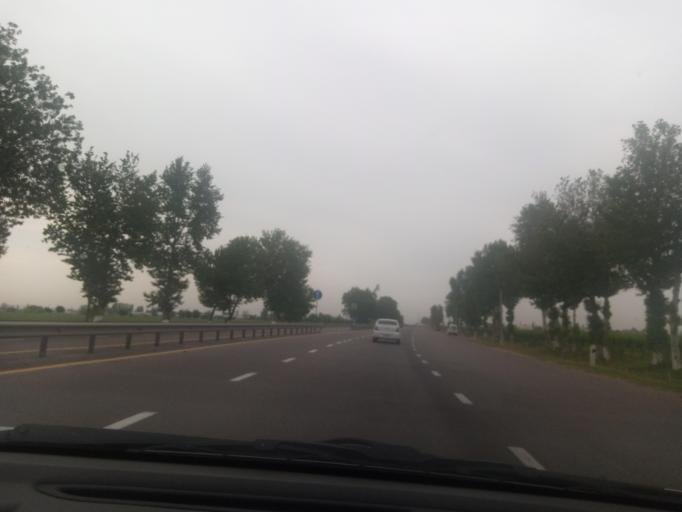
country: UZ
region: Toshkent Shahri
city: Bektemir
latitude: 41.1433
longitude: 69.4321
